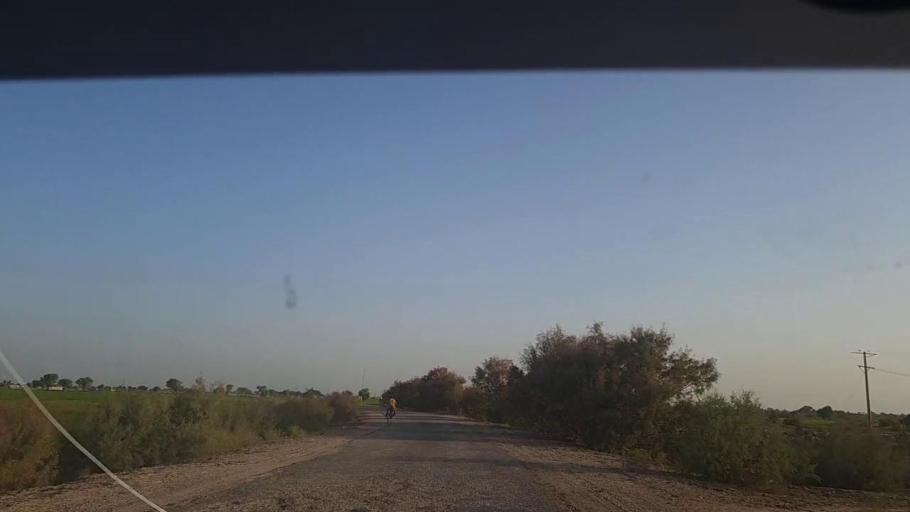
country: PK
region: Sindh
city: Thul
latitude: 28.1384
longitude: 68.8869
